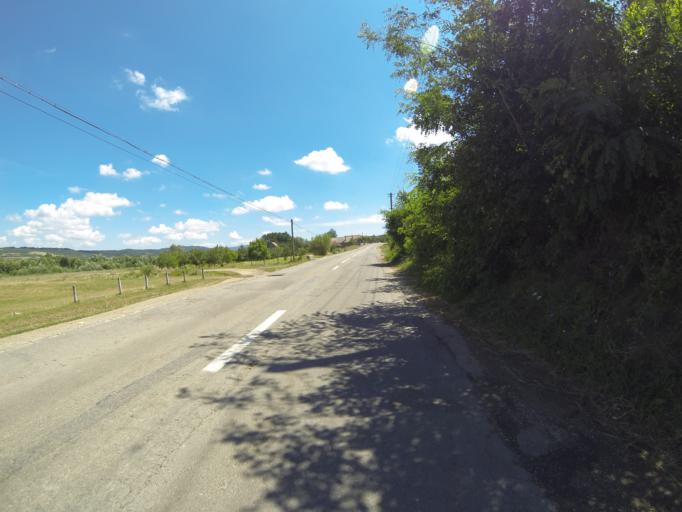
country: RO
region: Brasov
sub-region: Comuna Sinca Veche
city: Sinca Veche
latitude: 45.7570
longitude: 25.1748
